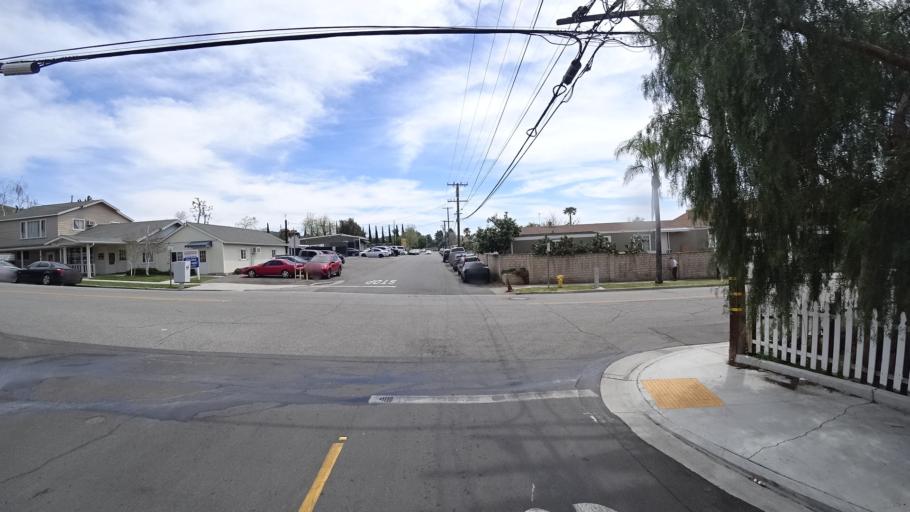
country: US
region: California
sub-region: Ventura County
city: Thousand Oaks
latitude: 34.1724
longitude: -118.8365
